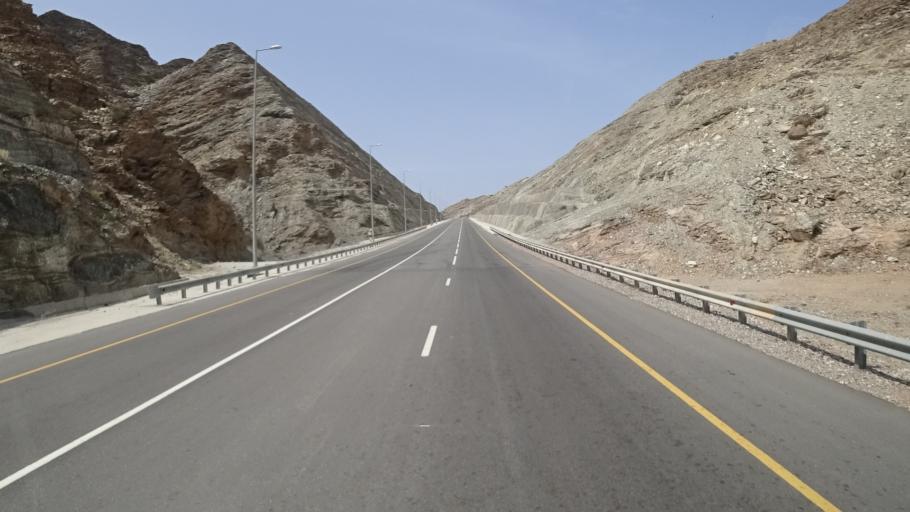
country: OM
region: Muhafazat Masqat
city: Muscat
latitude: 23.4391
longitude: 58.7583
